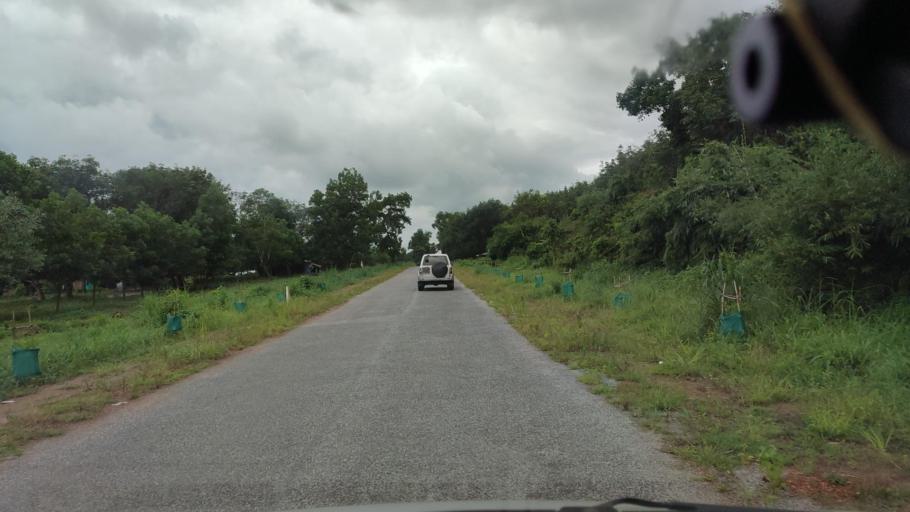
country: MM
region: Bago
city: Thanatpin
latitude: 17.2488
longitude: 96.3323
